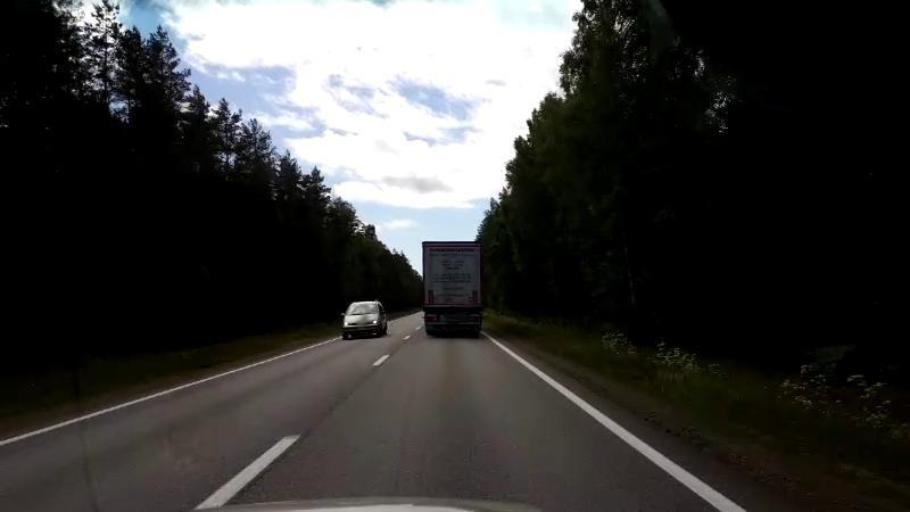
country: LV
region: Salacgrivas
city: Salacgriva
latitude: 57.5227
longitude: 24.4308
